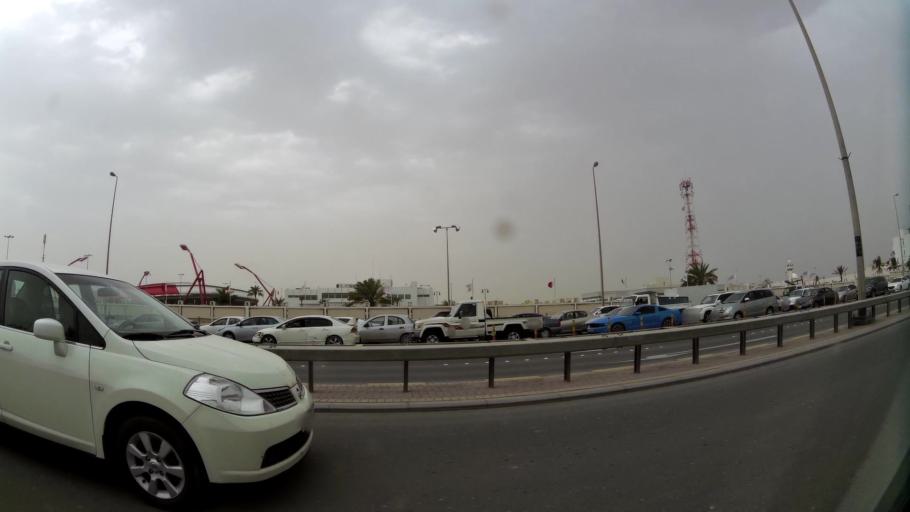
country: BH
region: Northern
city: Madinat `Isa
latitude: 26.1572
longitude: 50.5405
